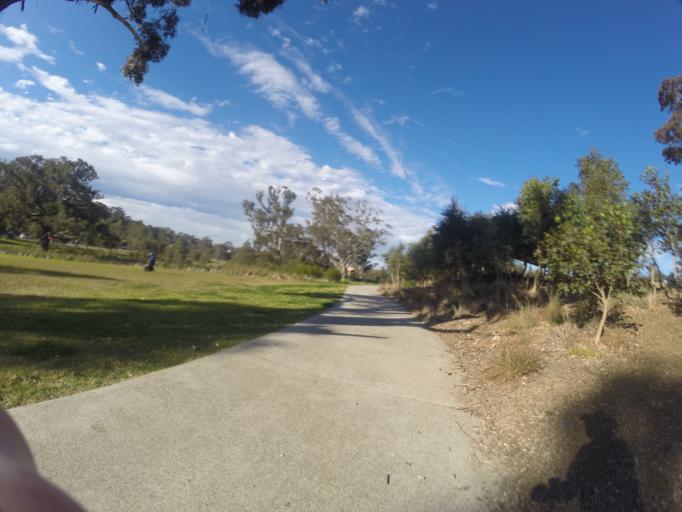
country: AU
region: New South Wales
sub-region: Fairfield
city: Horsley Park
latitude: -33.8511
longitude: 150.8721
